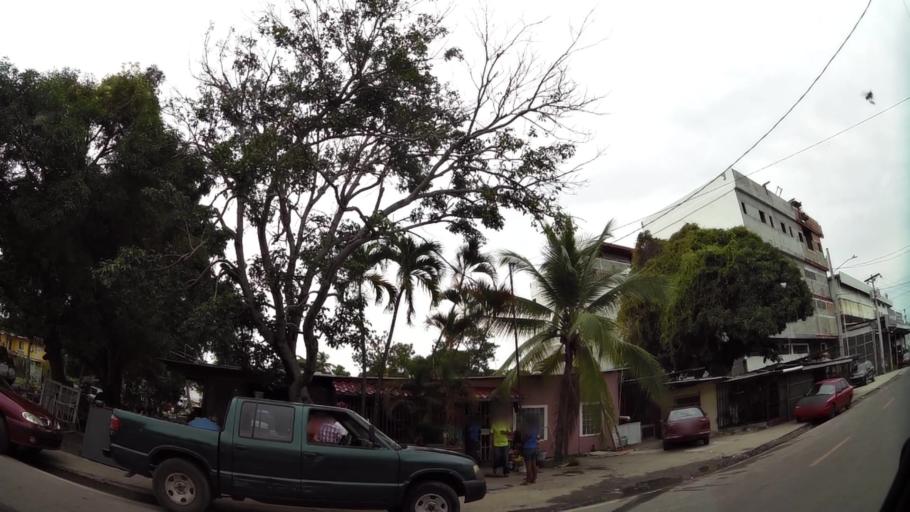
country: PA
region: Panama
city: San Miguelito
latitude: 9.0455
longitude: -79.4432
